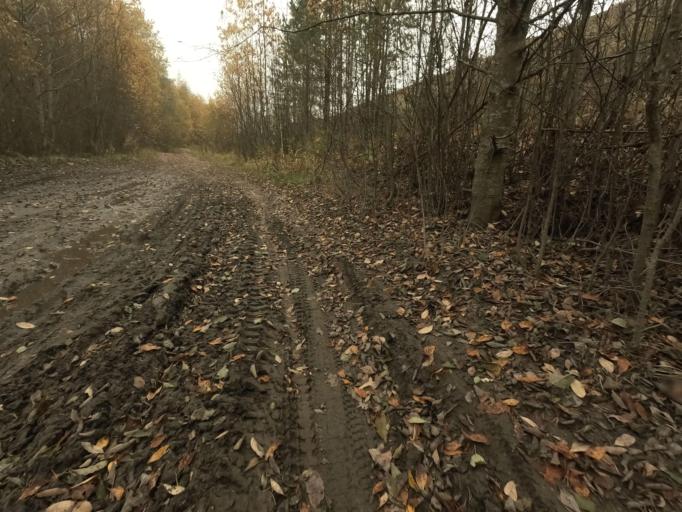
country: RU
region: Leningrad
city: Pavlovo
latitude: 59.7760
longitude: 30.9011
